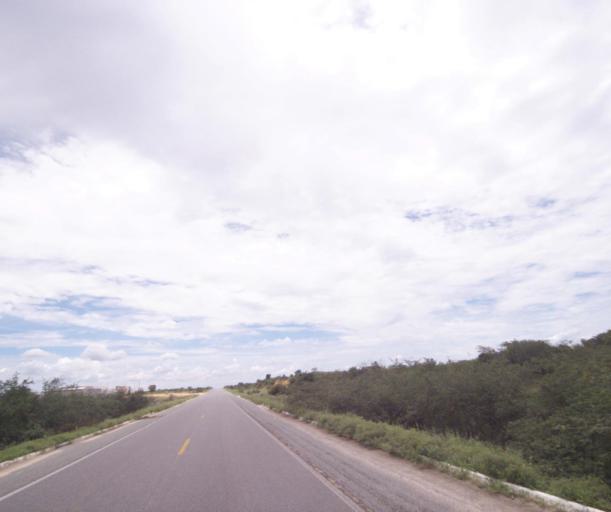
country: BR
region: Bahia
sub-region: Carinhanha
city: Carinhanha
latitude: -14.2967
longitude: -43.7855
